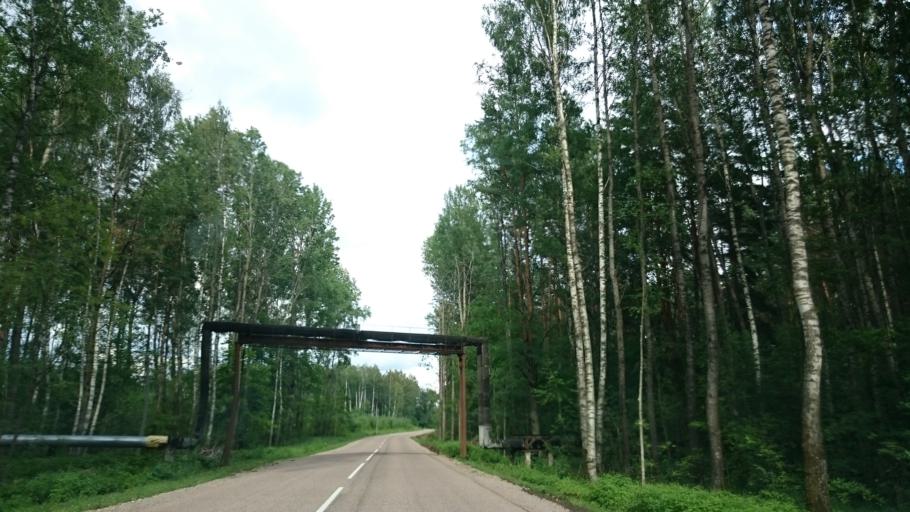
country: LV
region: Salaspils
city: Salaspils
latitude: 56.8683
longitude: 24.3922
